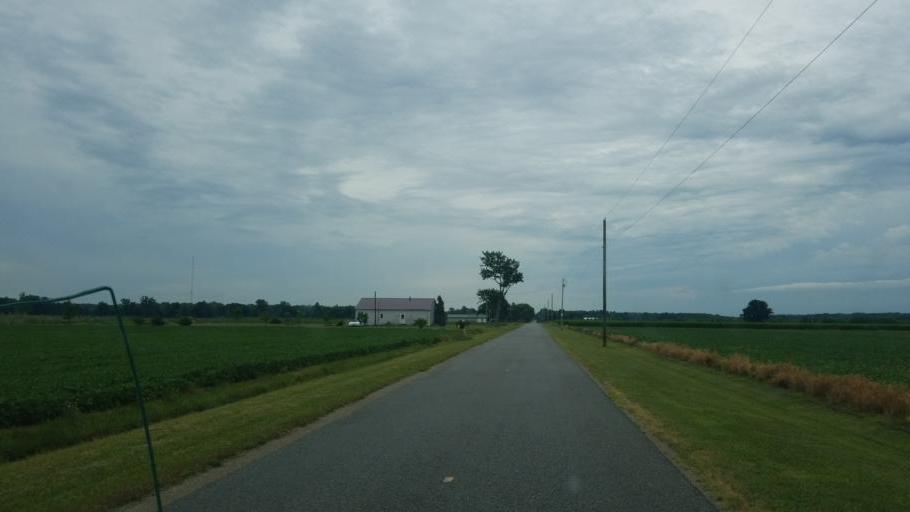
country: US
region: Ohio
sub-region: Defiance County
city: Hicksville
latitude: 41.2503
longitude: -84.6894
